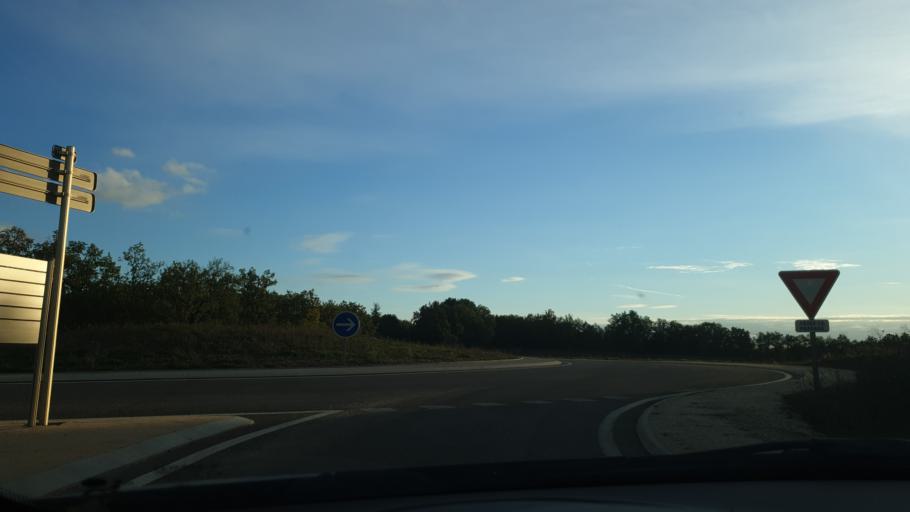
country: FR
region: Midi-Pyrenees
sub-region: Departement du Lot
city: Luzech
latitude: 44.4102
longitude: 1.2514
